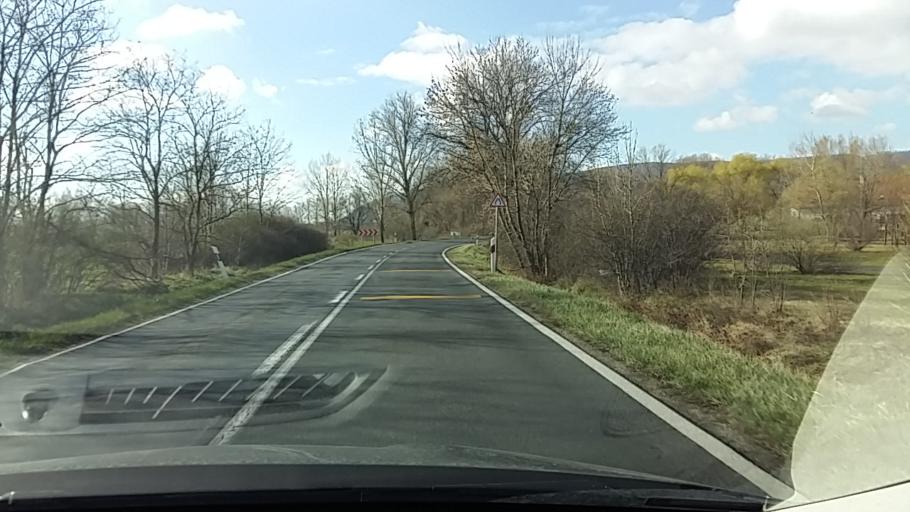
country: HU
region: Veszprem
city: Tapolca
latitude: 46.8516
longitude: 17.3814
